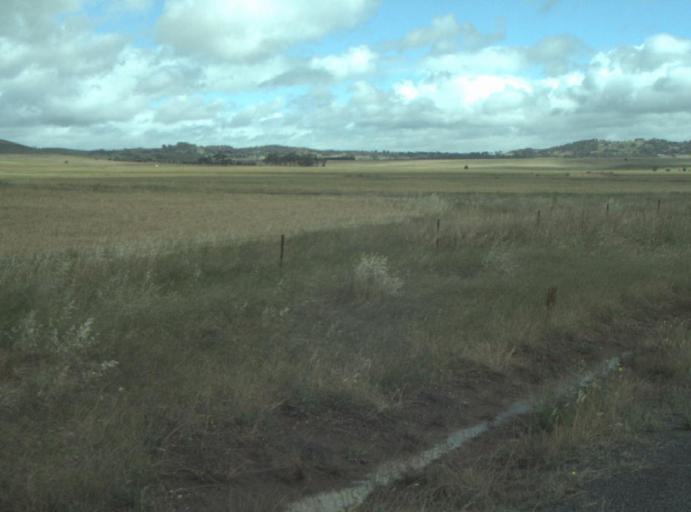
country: AU
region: Victoria
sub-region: Greater Geelong
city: Lara
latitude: -37.9120
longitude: 144.3153
